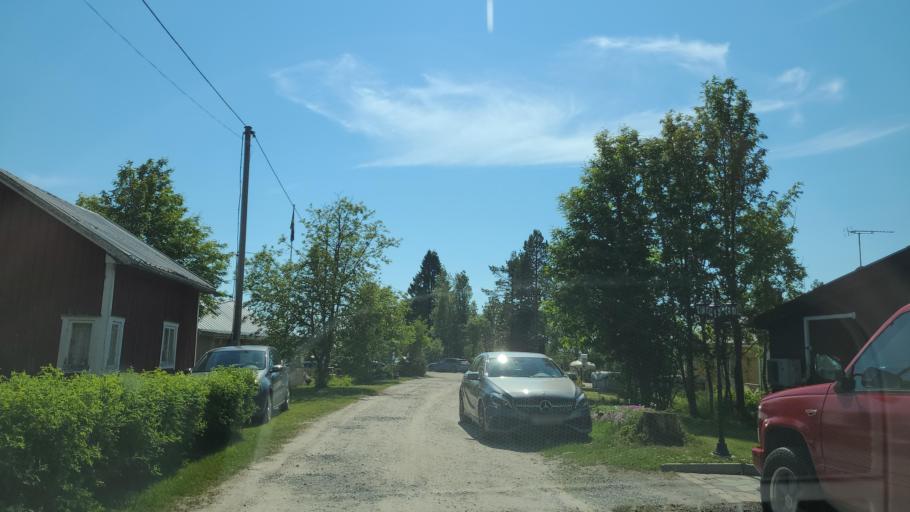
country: SE
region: Vaesterbotten
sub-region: Robertsfors Kommun
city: Robertsfors
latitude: 64.1430
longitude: 20.9646
